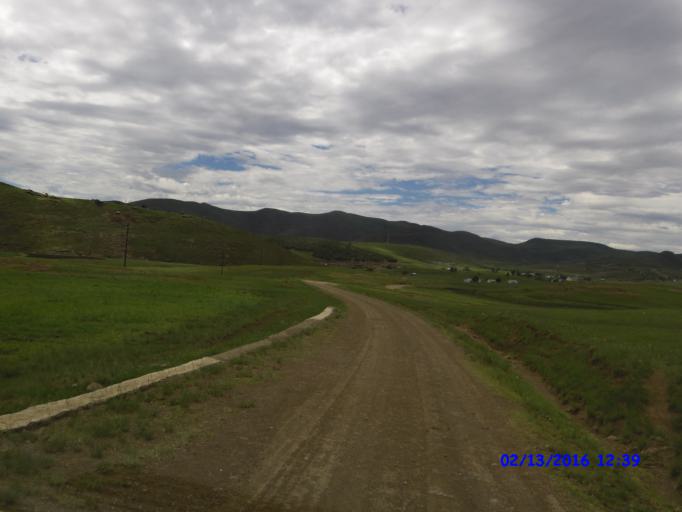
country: LS
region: Maseru
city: Nako
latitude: -29.8340
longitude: 28.0287
